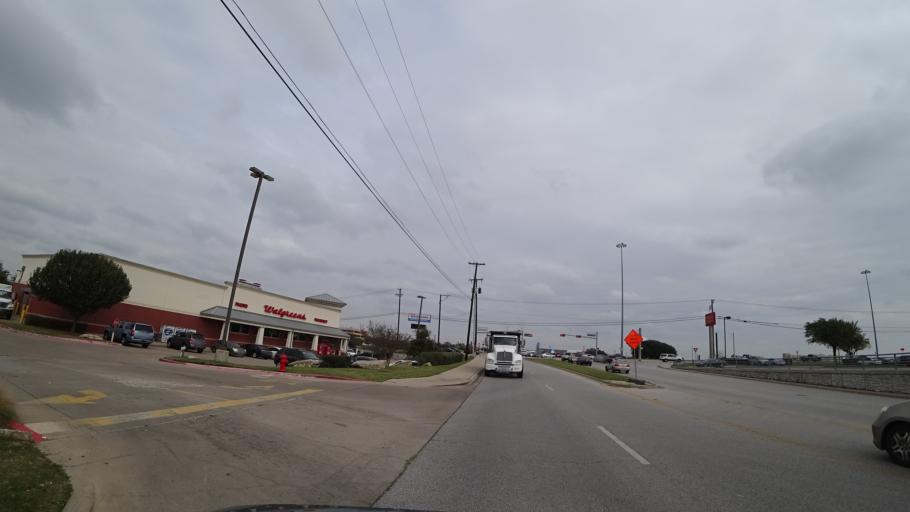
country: US
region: Texas
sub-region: Williamson County
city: Round Rock
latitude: 30.4882
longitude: -97.6786
